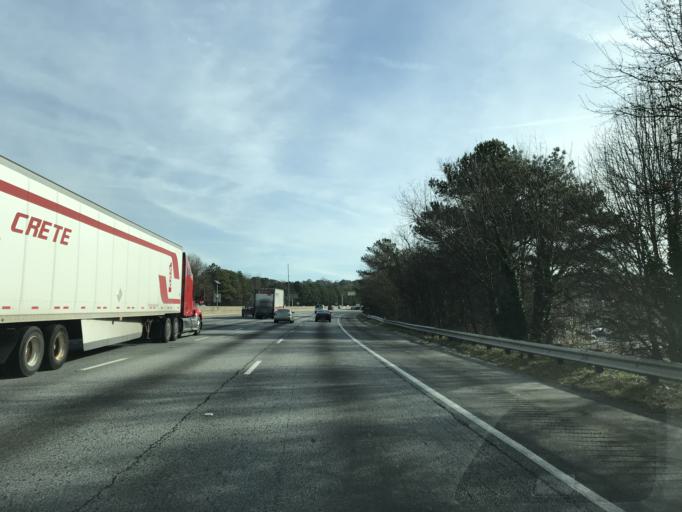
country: US
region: Georgia
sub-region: DeKalb County
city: Doraville
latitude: 33.9201
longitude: -84.2996
